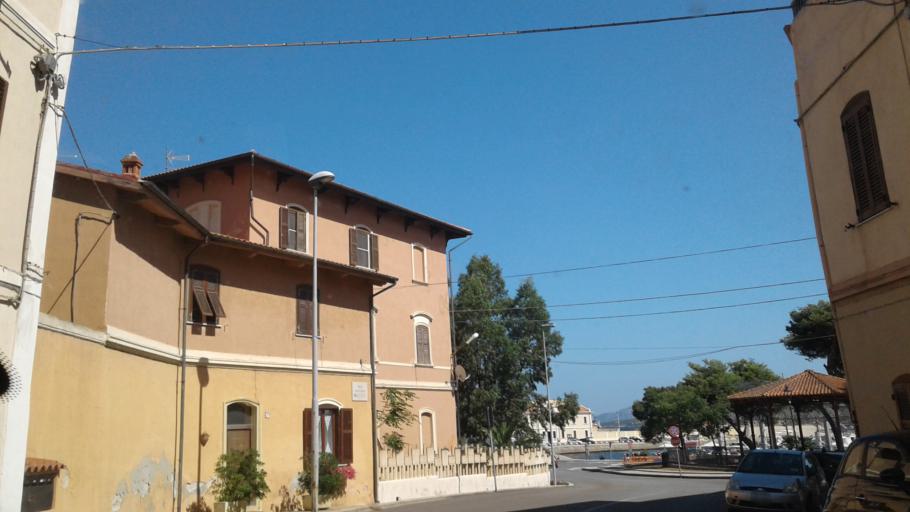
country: IT
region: Sardinia
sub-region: Provincia di Olbia-Tempio
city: La Maddalena
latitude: 41.2158
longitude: 9.4095
